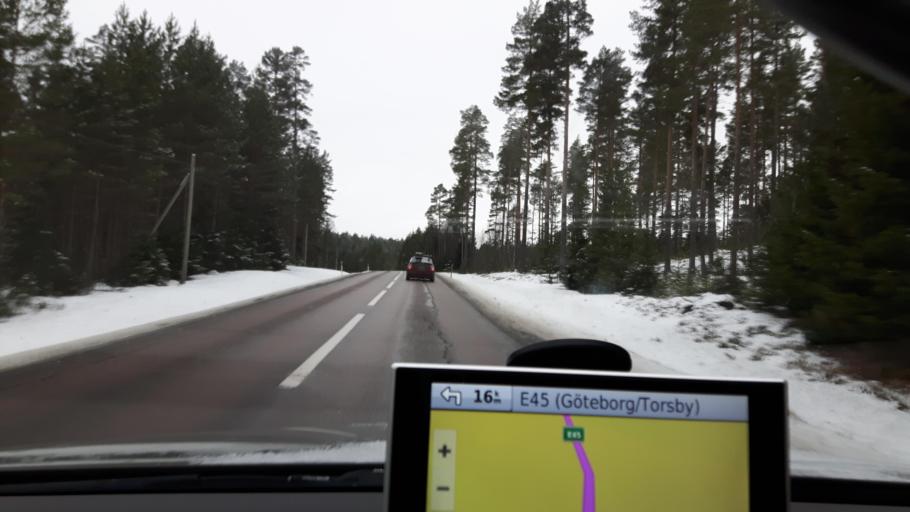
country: SE
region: Vaermland
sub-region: Torsby Kommun
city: Torsby
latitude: 60.3798
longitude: 13.2293
